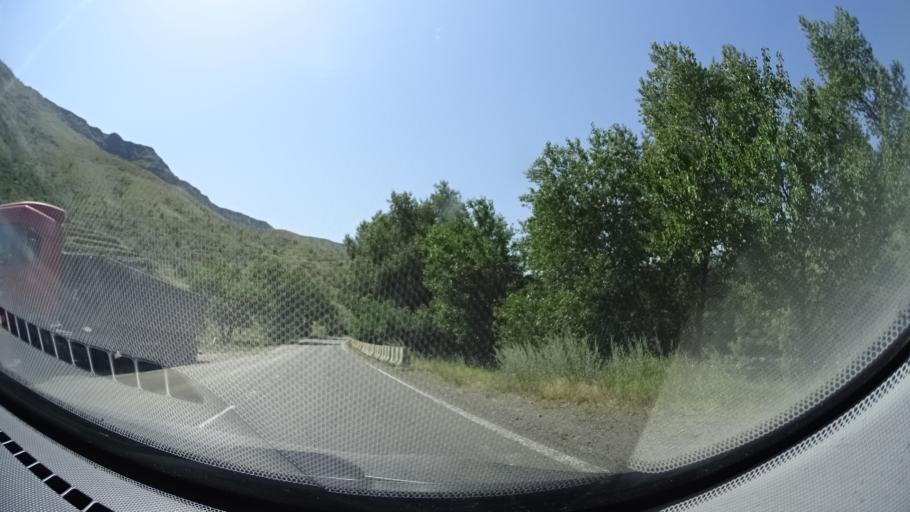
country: GE
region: Samtskhe-Javakheti
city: Aspindza
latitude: 41.5335
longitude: 43.2608
